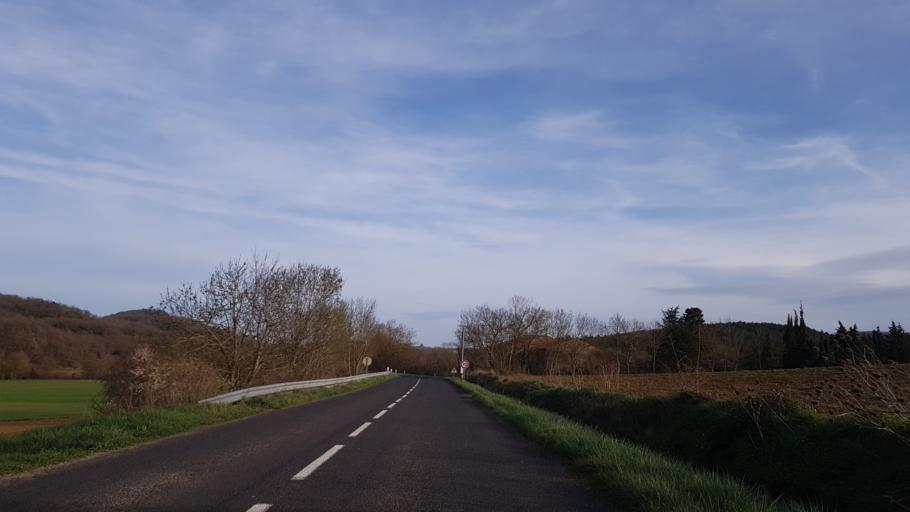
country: FR
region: Midi-Pyrenees
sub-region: Departement de l'Ariege
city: Mirepoix
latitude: 43.1784
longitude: 1.9138
